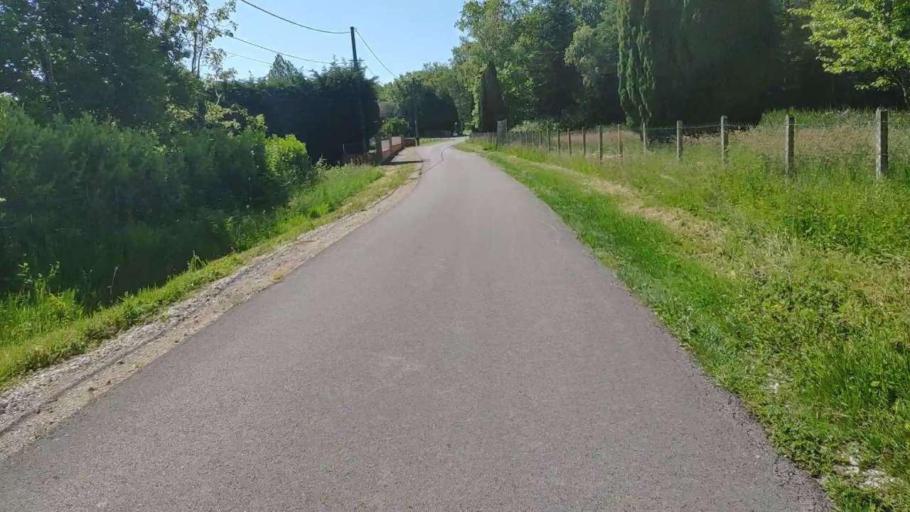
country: FR
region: Franche-Comte
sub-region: Departement du Jura
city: Bletterans
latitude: 46.7989
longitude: 5.4454
